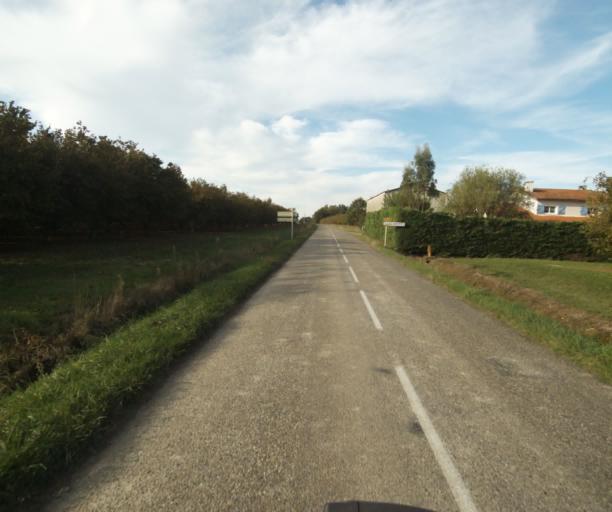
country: FR
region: Midi-Pyrenees
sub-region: Departement du Tarn-et-Garonne
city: Finhan
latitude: 43.9002
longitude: 1.1247
